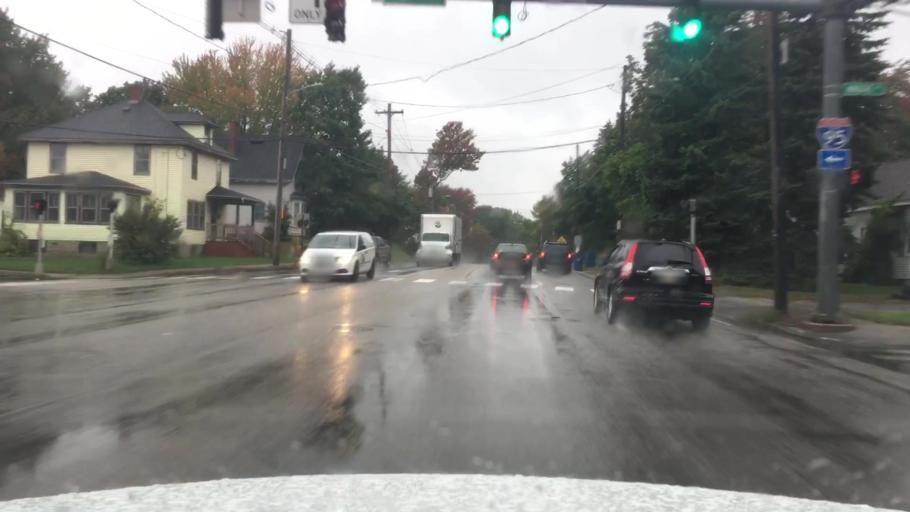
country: US
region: Maine
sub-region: Cumberland County
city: Portland
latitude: 43.6897
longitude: -70.2959
